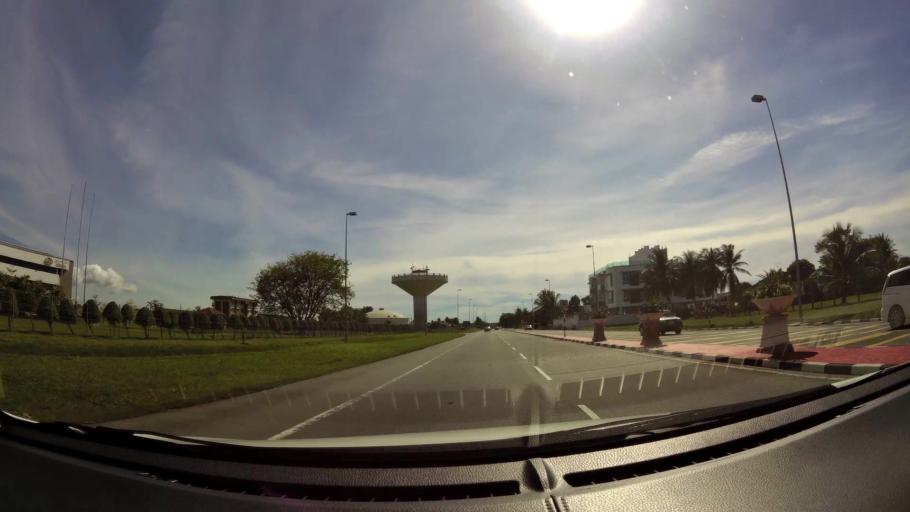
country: BN
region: Belait
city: Kuala Belait
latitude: 4.5789
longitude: 114.2113
